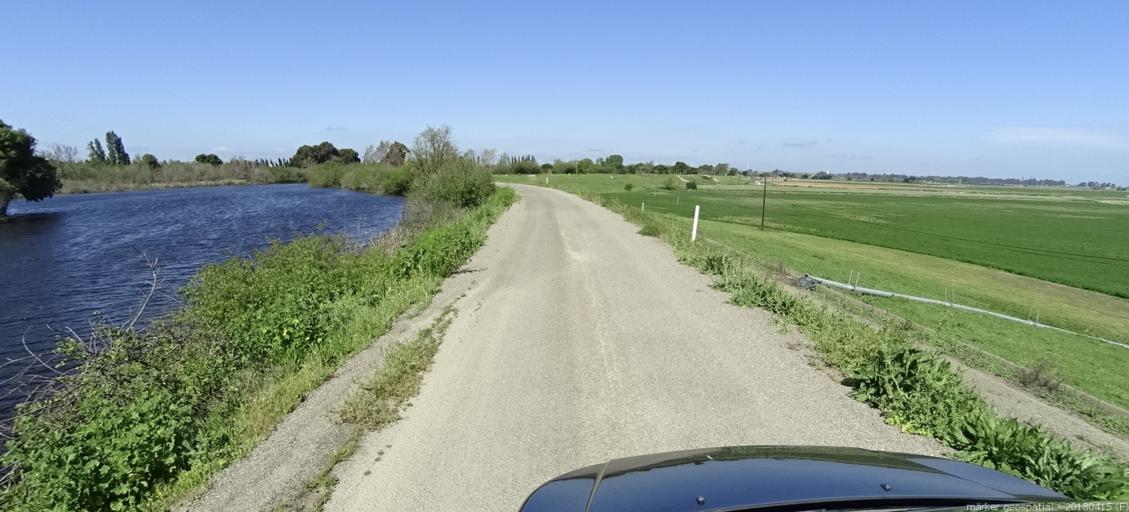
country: US
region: California
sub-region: Solano County
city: Rio Vista
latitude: 38.1203
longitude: -121.6593
